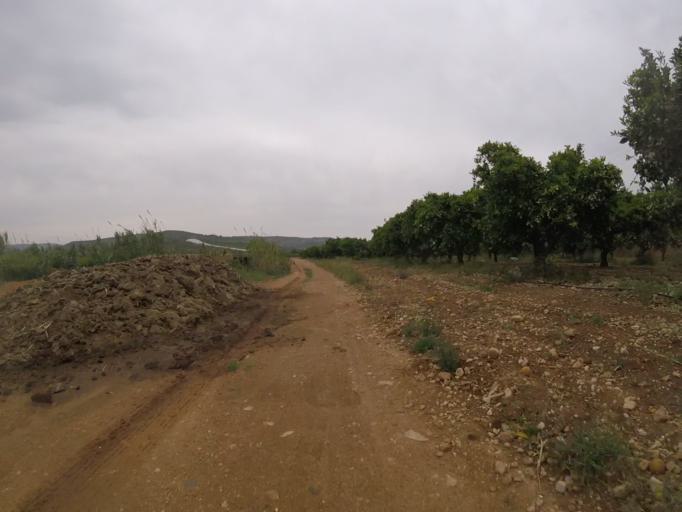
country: ES
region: Valencia
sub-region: Provincia de Castello
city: Alcoceber
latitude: 40.2657
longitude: 0.2578
